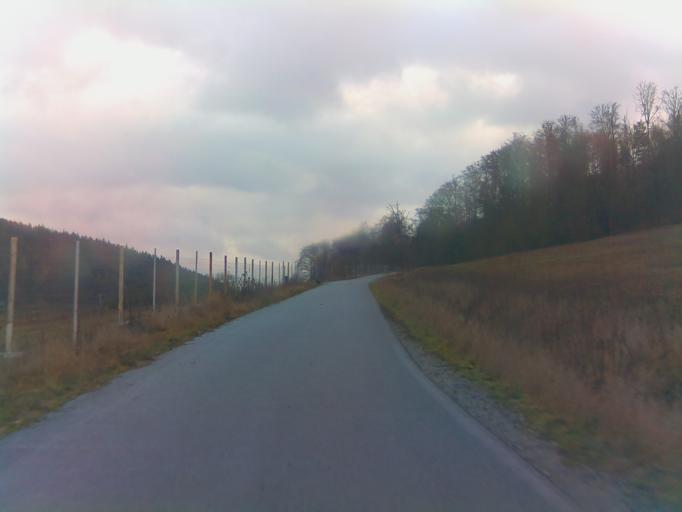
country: DE
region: Thuringia
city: Wolfershausen
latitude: 50.4657
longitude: 10.4367
